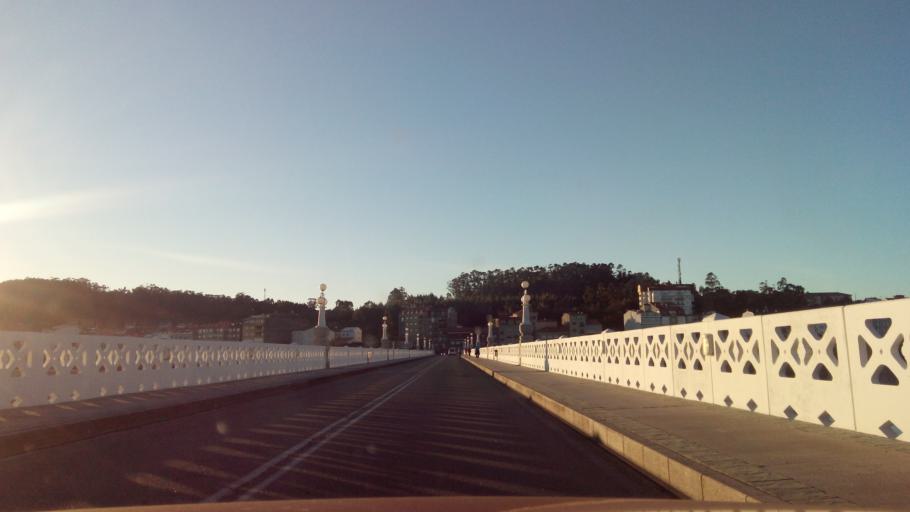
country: ES
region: Galicia
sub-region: Provincia de Pontevedra
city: O Grove
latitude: 42.4876
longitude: -8.8535
